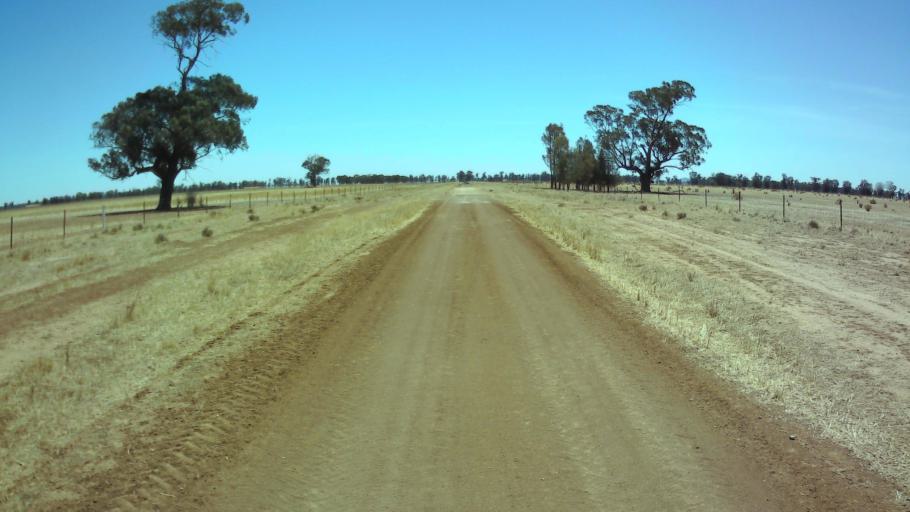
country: AU
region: New South Wales
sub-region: Weddin
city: Grenfell
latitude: -33.9862
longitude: 147.7351
